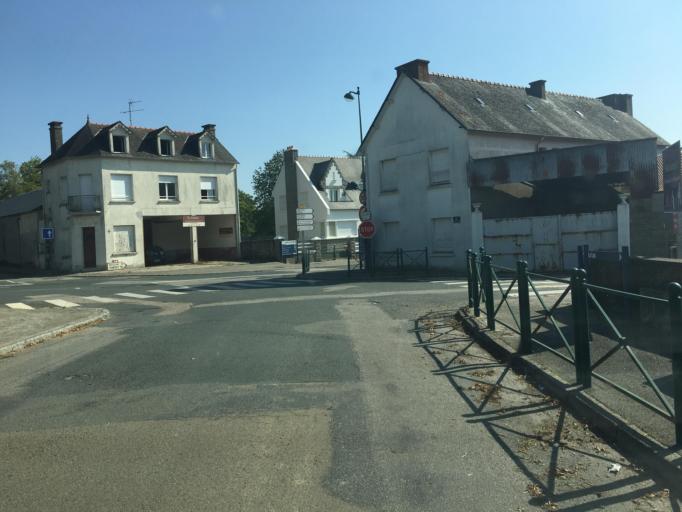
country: FR
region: Brittany
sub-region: Departement des Cotes-d'Armor
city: Mur-de-Bretagne
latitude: 48.2018
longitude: -2.9898
